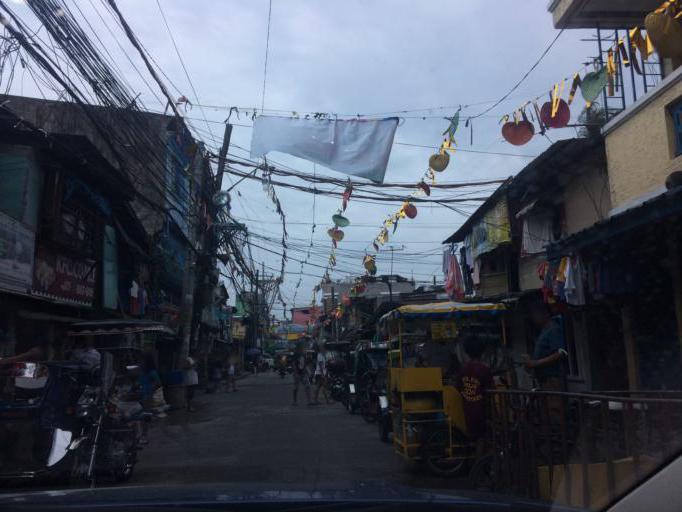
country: PH
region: Metro Manila
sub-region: Makati City
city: Makati City
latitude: 14.5449
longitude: 121.0026
